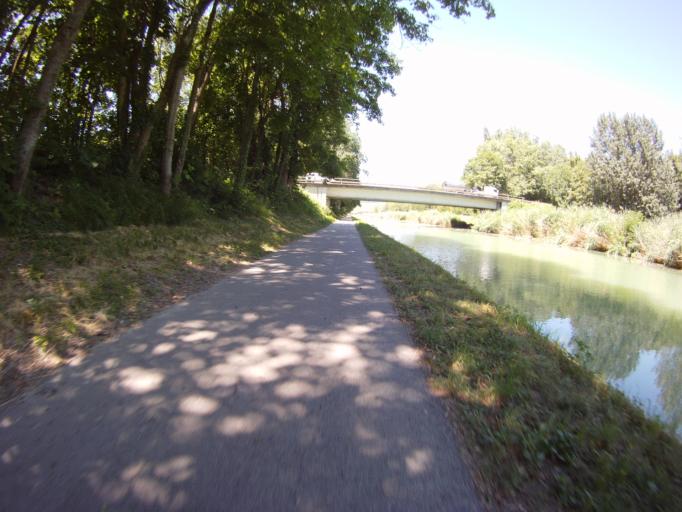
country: FR
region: Champagne-Ardenne
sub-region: Departement de la Marne
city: Dizy
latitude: 49.0617
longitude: 3.9587
